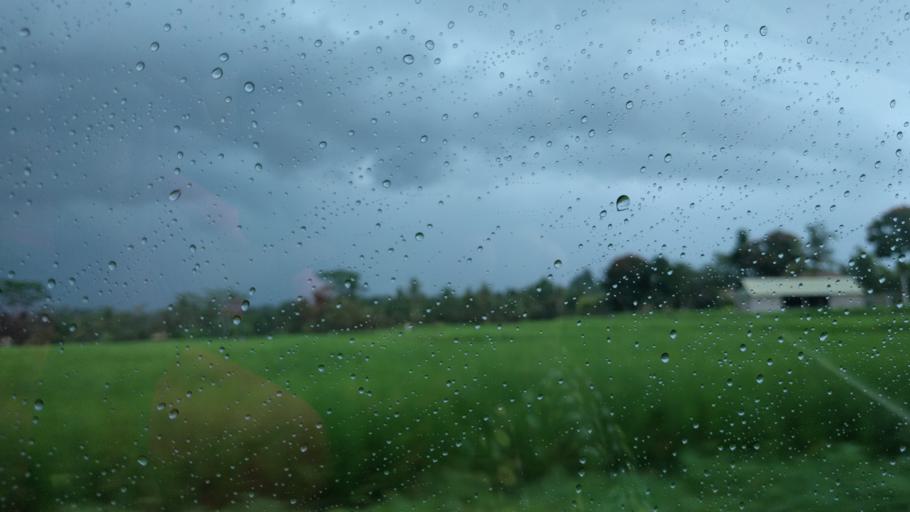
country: ID
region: Bali
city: Bunutan
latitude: -8.4801
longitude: 115.2583
